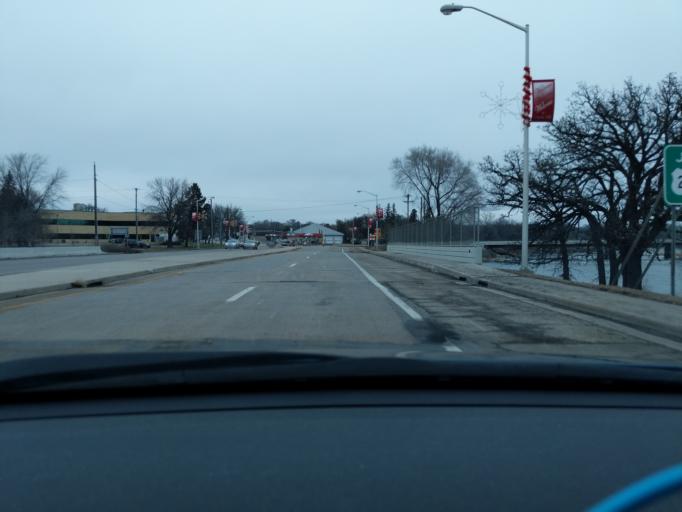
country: US
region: Minnesota
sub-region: Yellow Medicine County
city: Granite Falls
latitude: 44.8036
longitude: -95.5466
